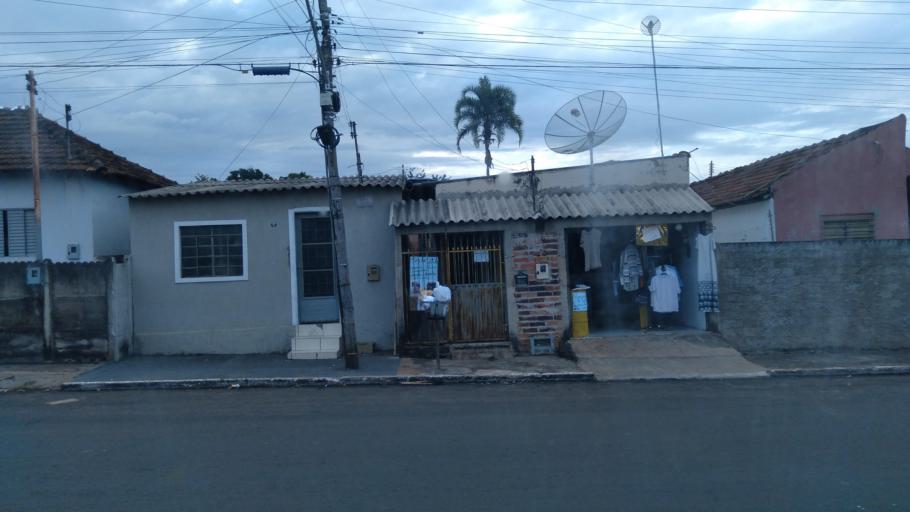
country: BR
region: Goias
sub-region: Mineiros
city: Mineiros
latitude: -17.5671
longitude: -52.5468
